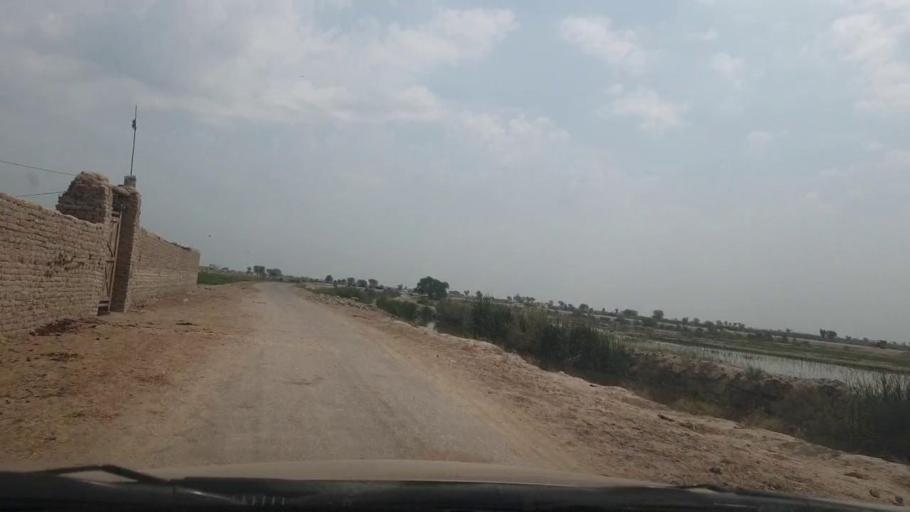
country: PK
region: Sindh
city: Ratodero
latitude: 27.7082
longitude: 68.2719
